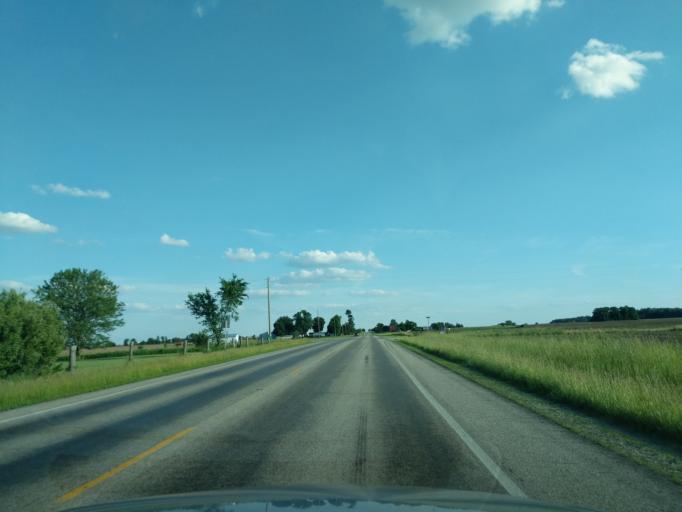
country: US
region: Indiana
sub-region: Huntington County
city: Roanoke
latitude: 40.9910
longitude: -85.4717
